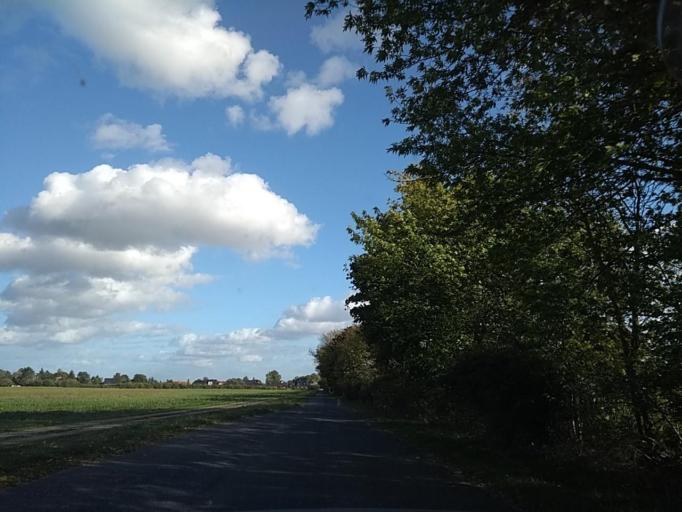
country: DE
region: Mecklenburg-Vorpommern
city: Ostseebad Dierhagen
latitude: 54.2340
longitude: 12.3781
